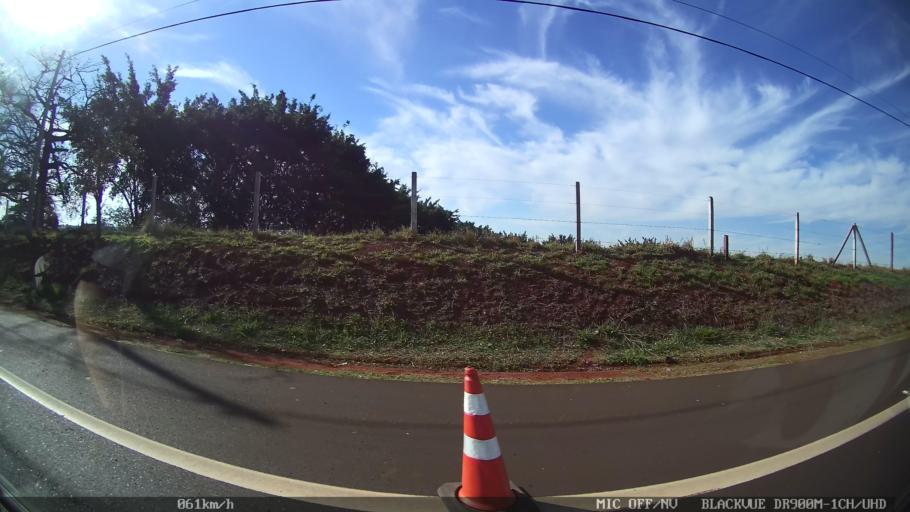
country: BR
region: Sao Paulo
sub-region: Araraquara
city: Araraquara
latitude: -21.7904
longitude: -48.1373
